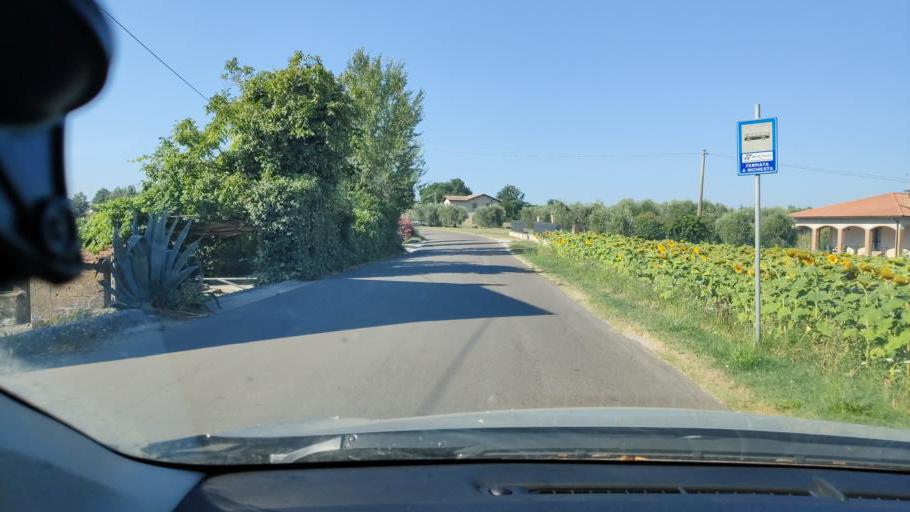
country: IT
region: Umbria
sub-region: Provincia di Terni
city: Fornole
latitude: 42.5321
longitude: 12.4492
